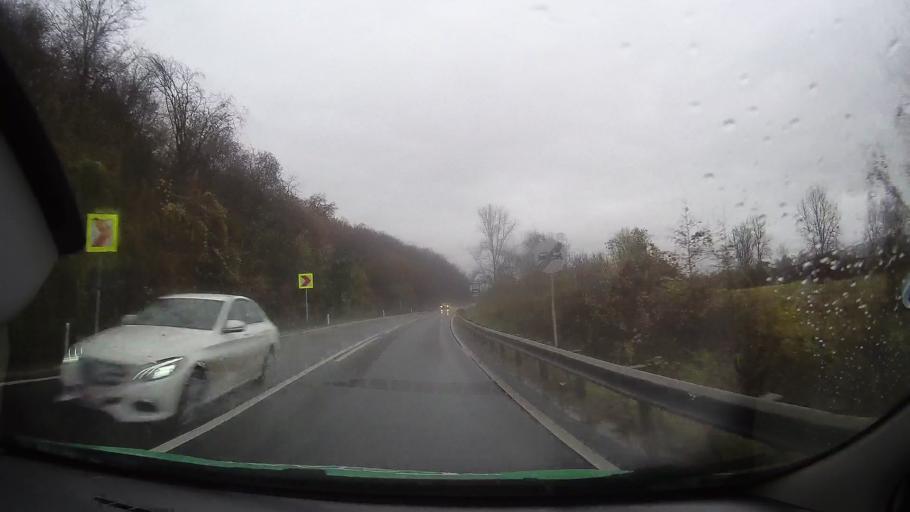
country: RO
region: Mures
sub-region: Comuna Brancovenesti
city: Brancovenesti
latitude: 46.8673
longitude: 24.7691
